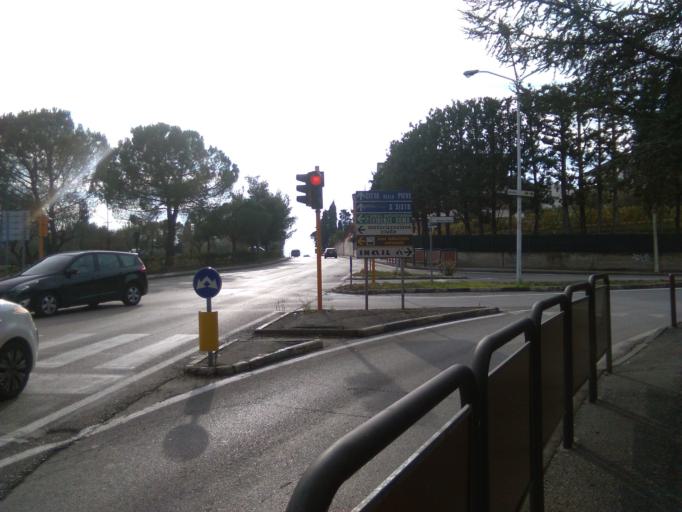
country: IT
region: Umbria
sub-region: Provincia di Perugia
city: Perugia
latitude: 43.0992
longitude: 12.3649
